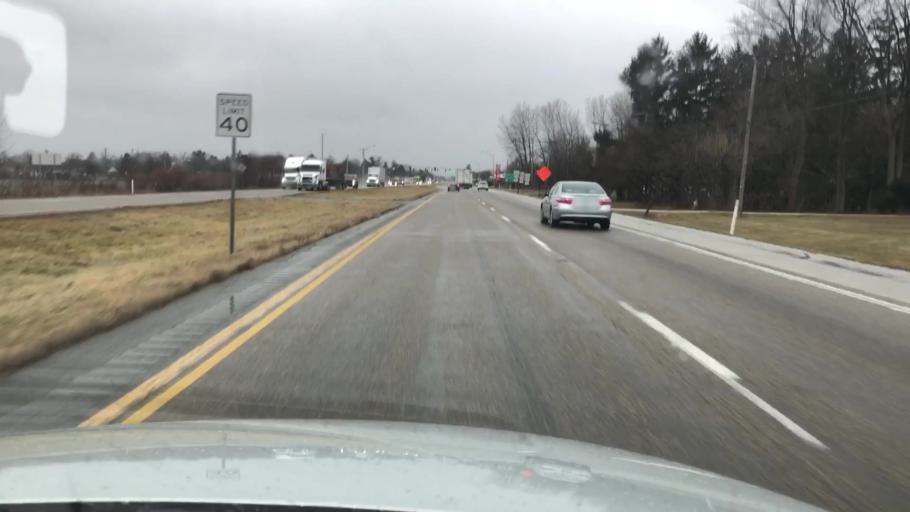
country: US
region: Indiana
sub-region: LaPorte County
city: Wanatah
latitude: 41.4341
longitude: -86.8875
